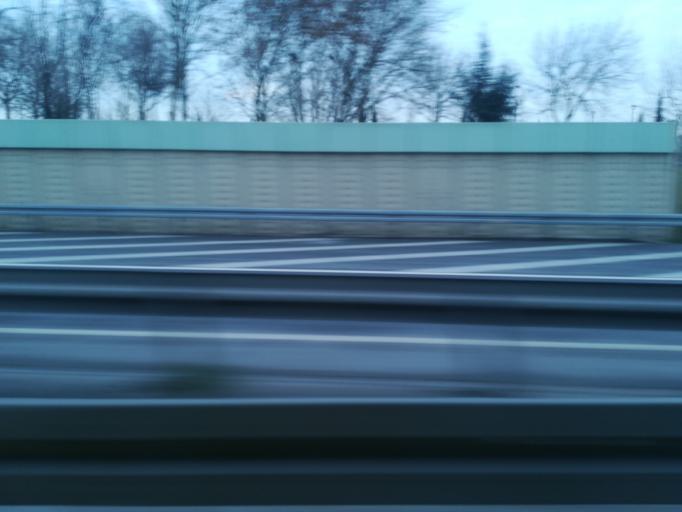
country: TR
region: Istanbul
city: Istanbul
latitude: 41.0276
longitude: 28.9256
